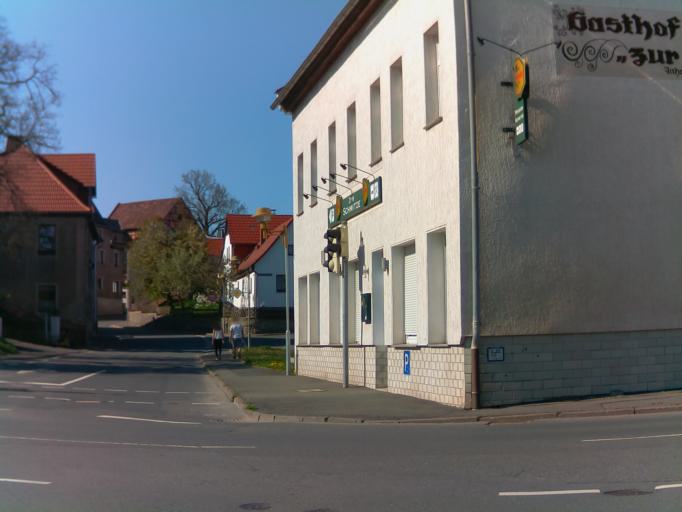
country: DE
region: Thuringia
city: Triptis
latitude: 50.7363
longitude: 11.8615
